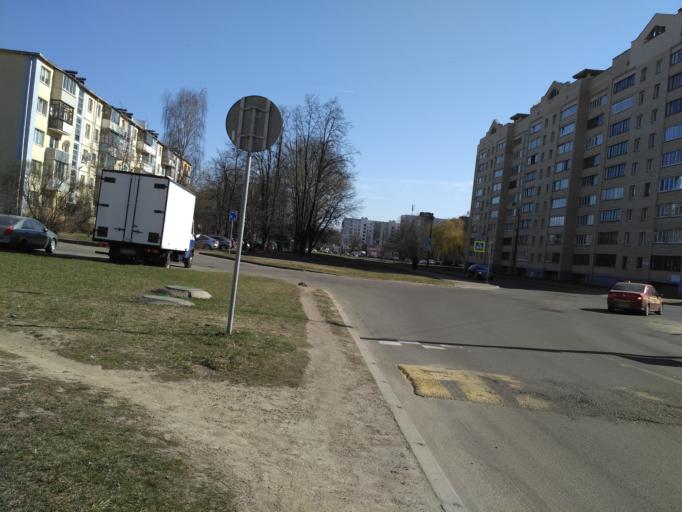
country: BY
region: Minsk
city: Novoye Medvezhino
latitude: 53.9041
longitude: 27.5035
